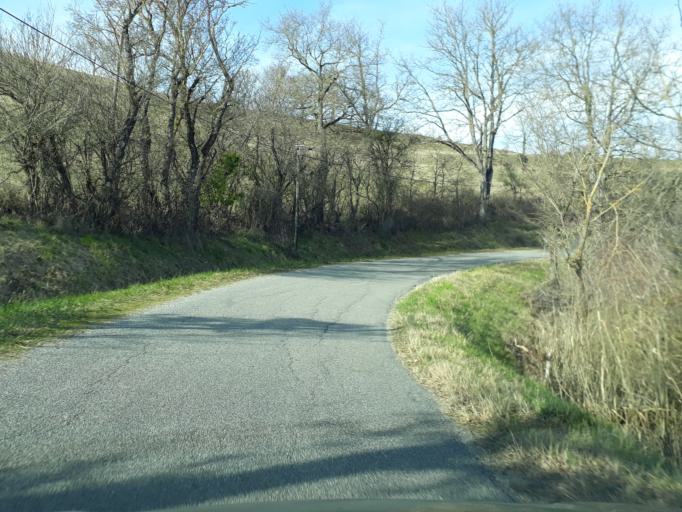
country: FR
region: Midi-Pyrenees
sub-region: Departement de la Haute-Garonne
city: Montesquieu-Volvestre
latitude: 43.1794
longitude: 1.2894
